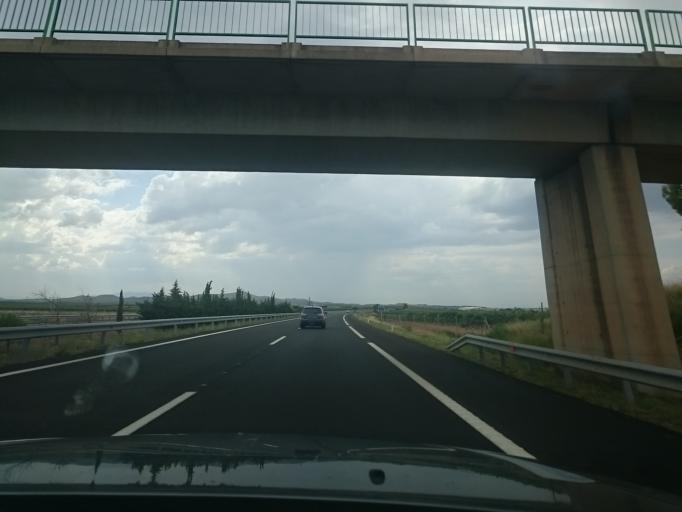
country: ES
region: La Rioja
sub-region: Provincia de La Rioja
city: Aldeanueva de Ebro
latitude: 42.2134
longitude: -1.8831
